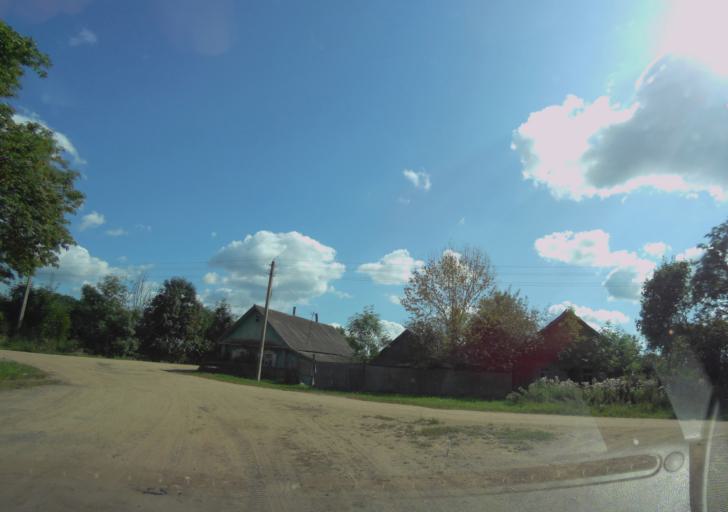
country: BY
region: Minsk
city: Zyembin
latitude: 54.4098
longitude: 28.3862
